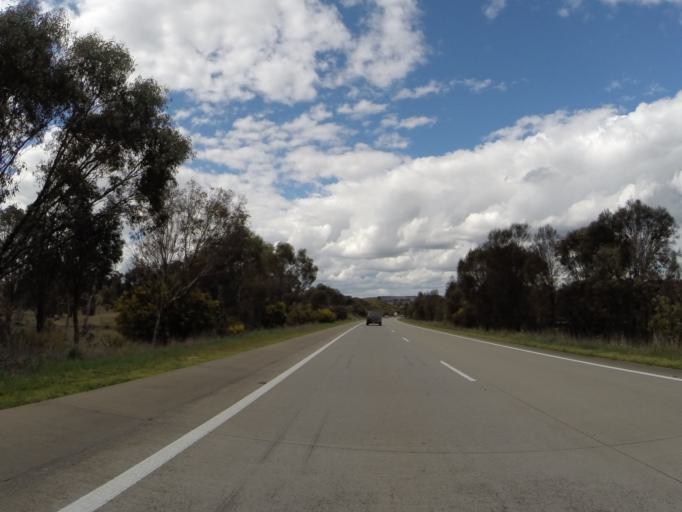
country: AU
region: New South Wales
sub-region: Yass Valley
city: Murrumbateman
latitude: -34.8138
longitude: 149.1113
